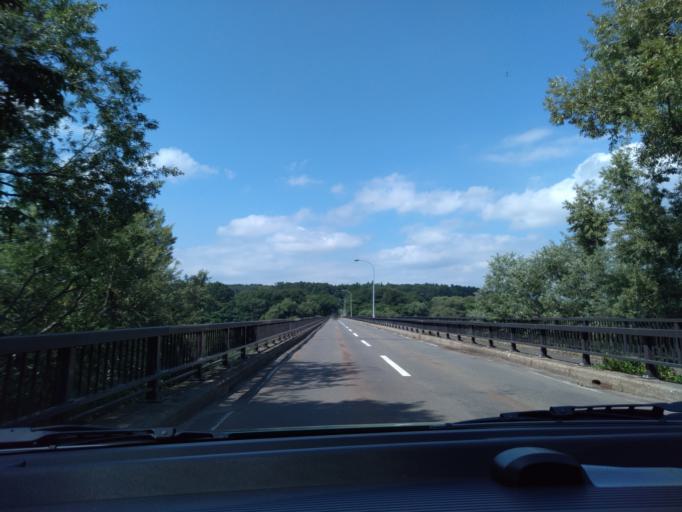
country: JP
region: Iwate
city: Shizukuishi
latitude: 39.6658
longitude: 140.9822
